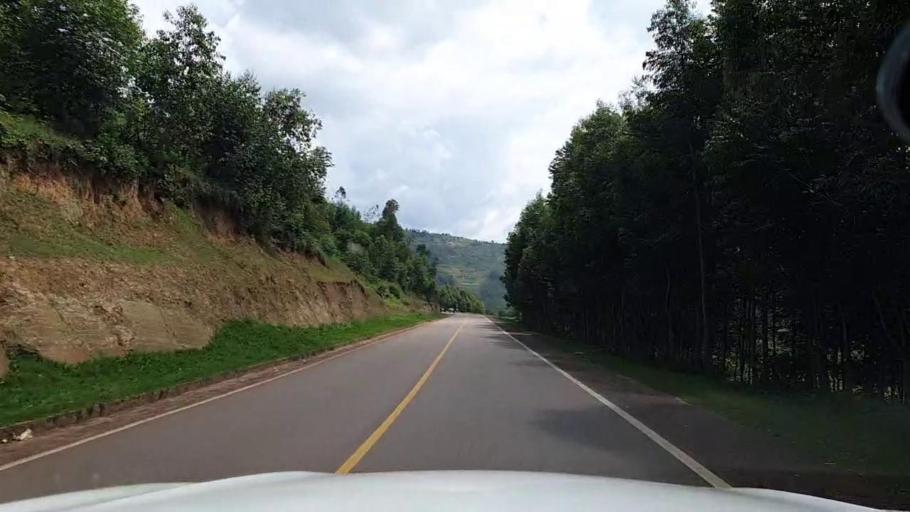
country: RW
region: Kigali
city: Kigali
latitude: -1.8176
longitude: 30.0909
